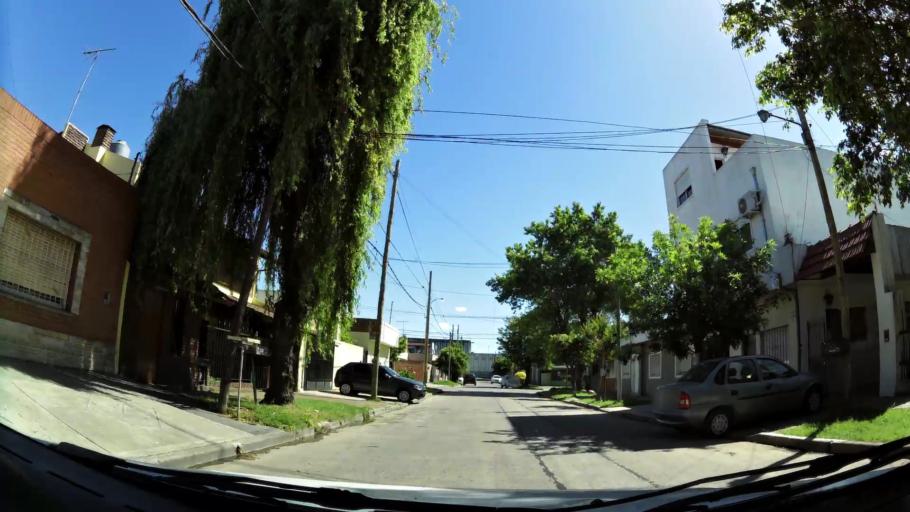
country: AR
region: Buenos Aires
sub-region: Partido de General San Martin
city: General San Martin
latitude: -34.5204
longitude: -58.5722
